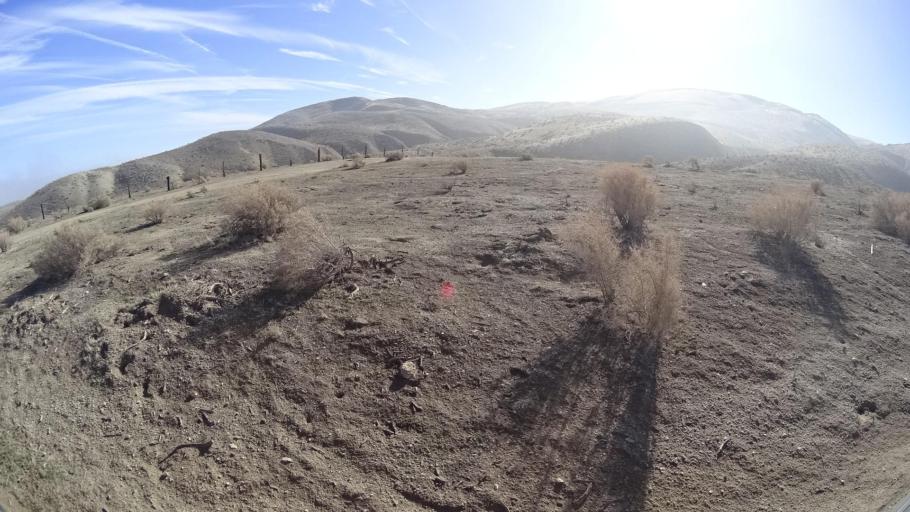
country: US
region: California
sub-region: Kern County
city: Maricopa
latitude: 35.0144
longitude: -119.4536
